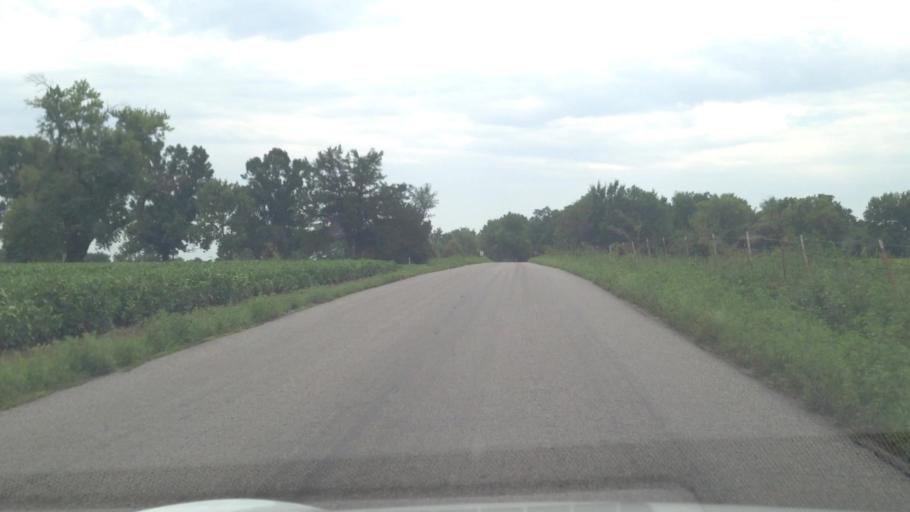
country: US
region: Kansas
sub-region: Crawford County
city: Girard
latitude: 37.5013
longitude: -94.8699
